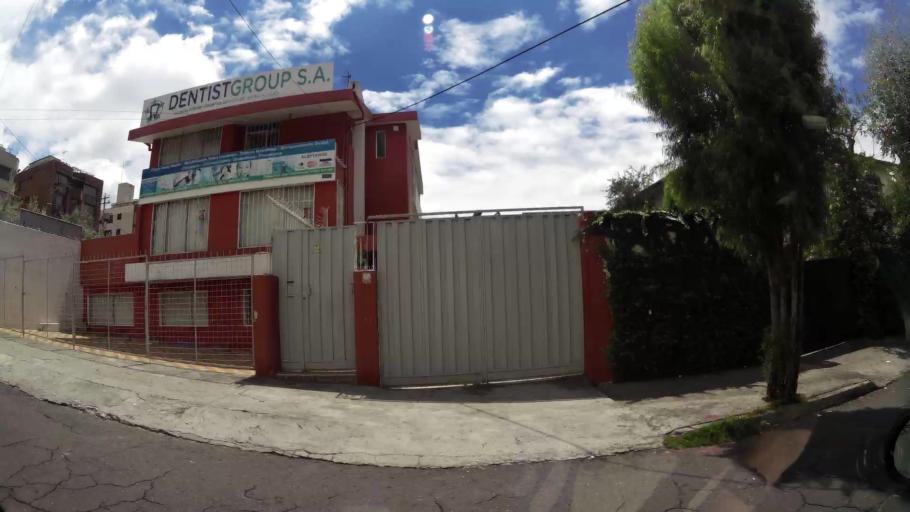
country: EC
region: Pichincha
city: Quito
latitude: -0.1774
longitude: -78.4907
